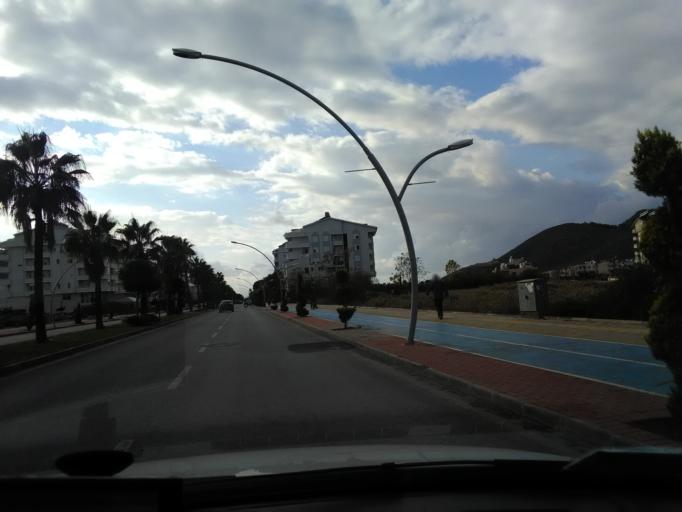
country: TR
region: Antalya
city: Gazipasa
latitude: 36.2670
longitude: 32.3041
